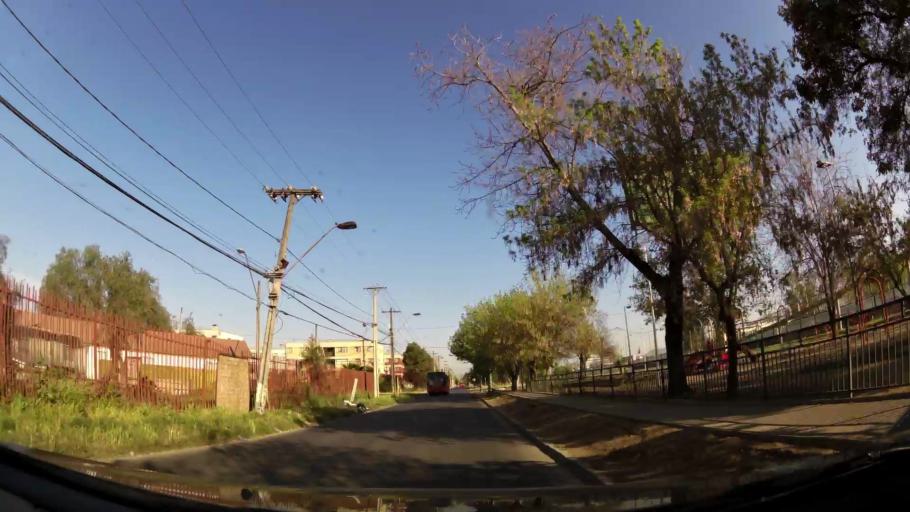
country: CL
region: Santiago Metropolitan
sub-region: Provincia de Santiago
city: Santiago
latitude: -33.3754
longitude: -70.6615
